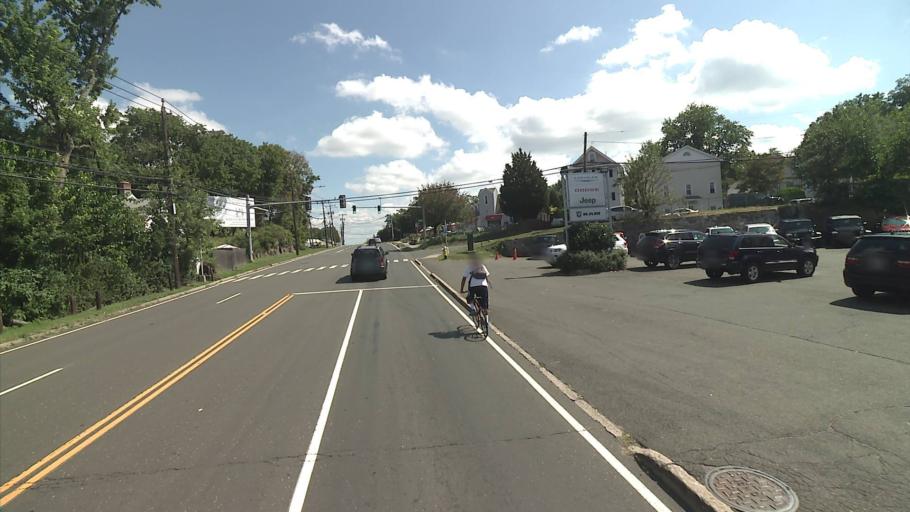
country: US
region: Connecticut
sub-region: Fairfield County
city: Greenwich
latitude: 41.0203
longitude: -73.6425
